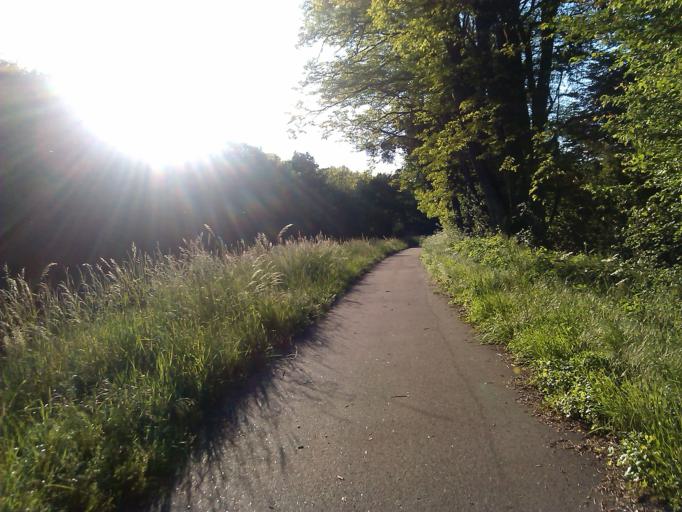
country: FR
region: Auvergne
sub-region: Departement de l'Allier
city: Dompierre-sur-Besbre
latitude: 46.5326
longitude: 3.7183
